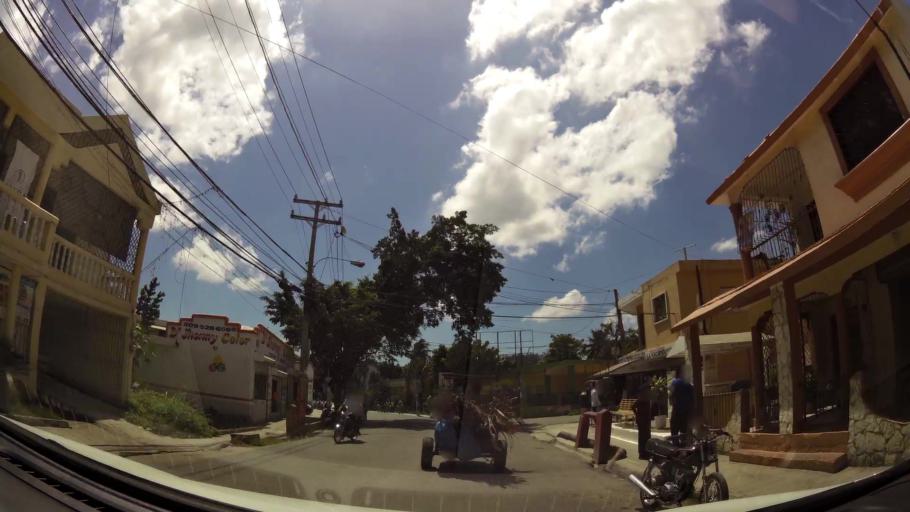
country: DO
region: San Cristobal
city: San Cristobal
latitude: 18.4050
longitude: -70.1071
